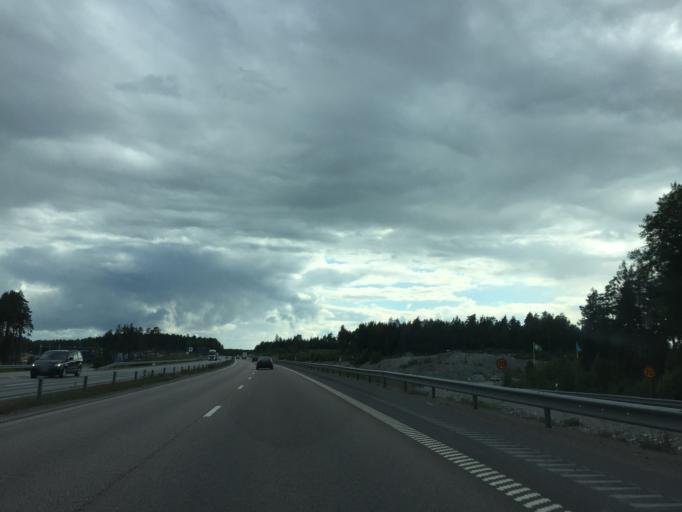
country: SE
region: Vaestmanland
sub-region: Vasteras
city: Vasteras
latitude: 59.6015
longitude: 16.4403
